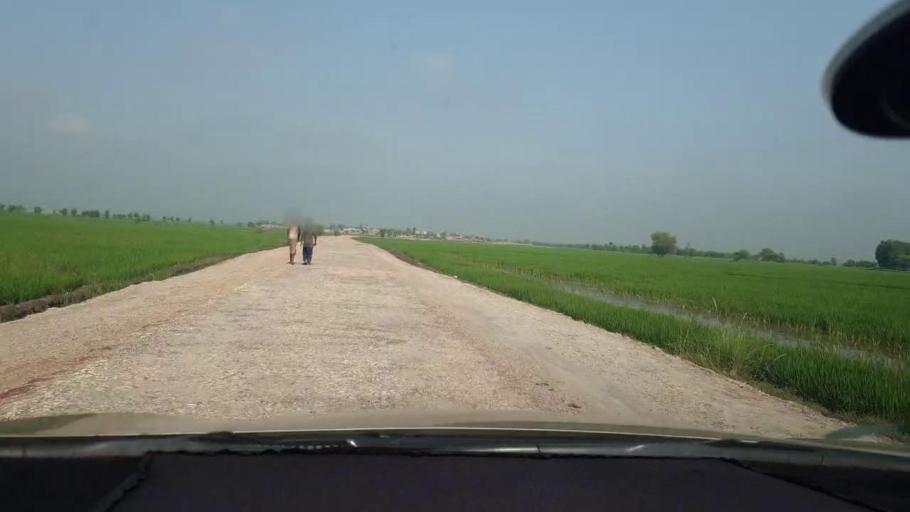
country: PK
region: Sindh
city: Kambar
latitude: 27.5386
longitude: 68.0547
